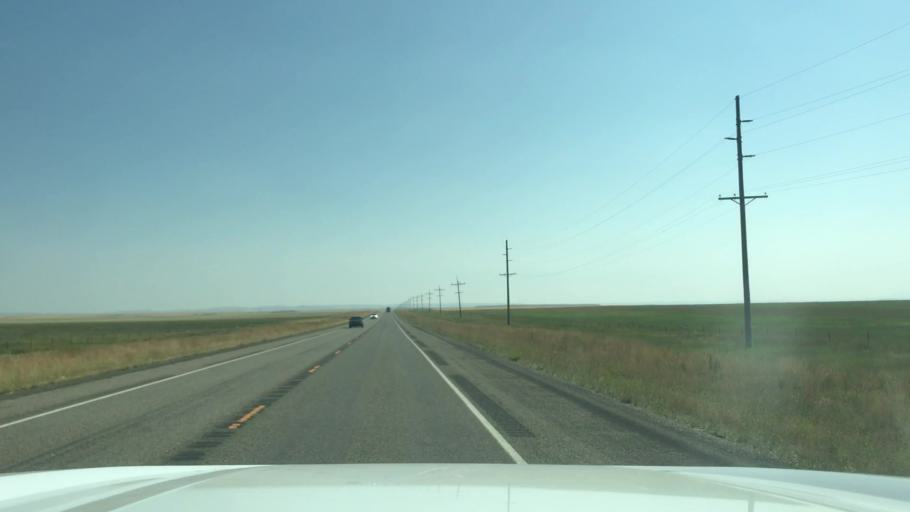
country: US
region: Montana
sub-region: Wheatland County
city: Harlowton
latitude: 46.5166
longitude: -109.7660
